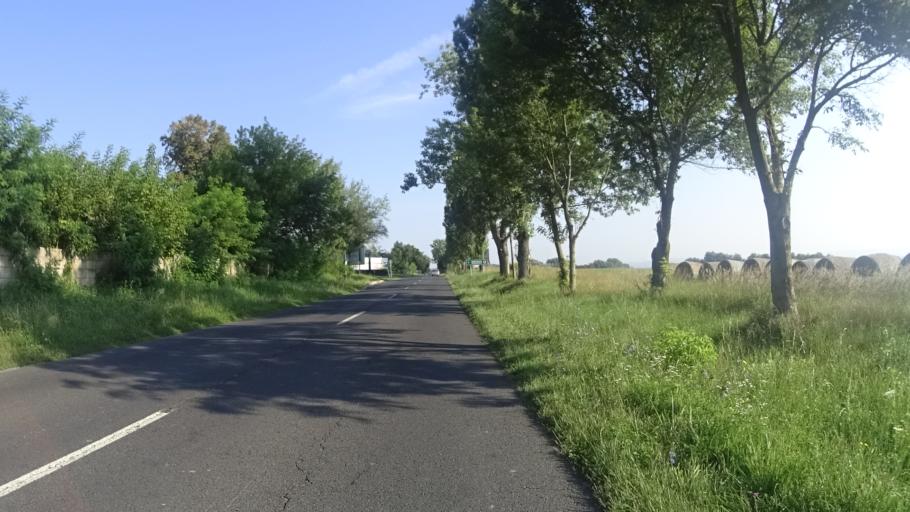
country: HU
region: Zala
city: Sarmellek
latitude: 46.6895
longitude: 17.1685
